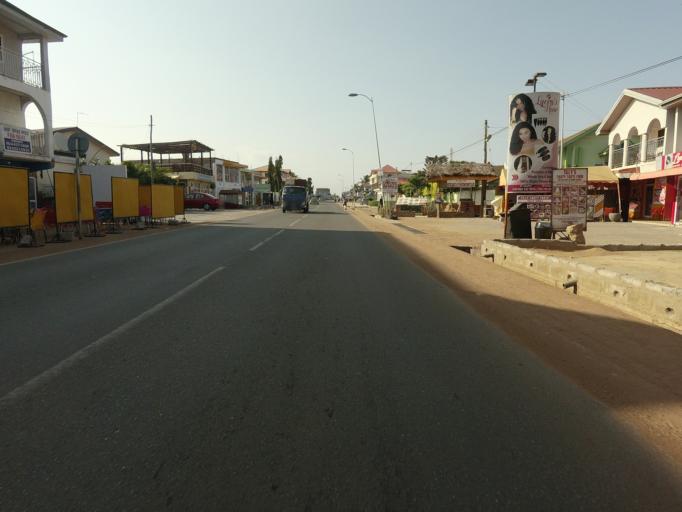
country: GH
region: Greater Accra
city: Nungua
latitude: 5.6280
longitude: -0.0762
